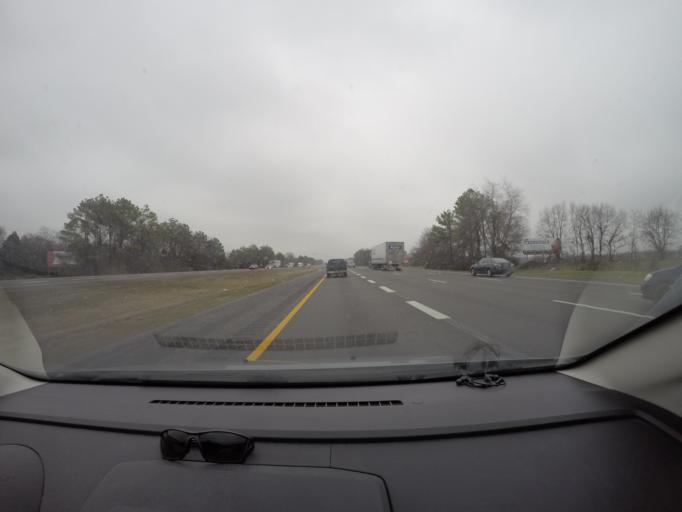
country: US
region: Tennessee
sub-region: Rutherford County
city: Smyrna
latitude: 35.8983
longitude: -86.4915
